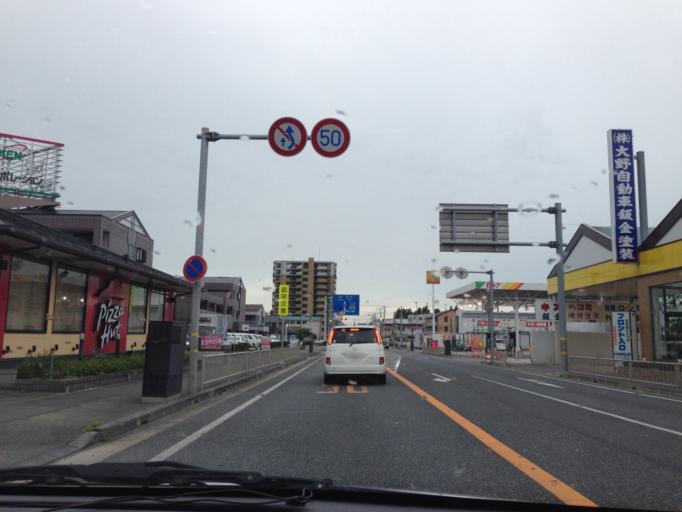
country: JP
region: Ibaraki
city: Naka
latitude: 36.0086
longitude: 140.1556
